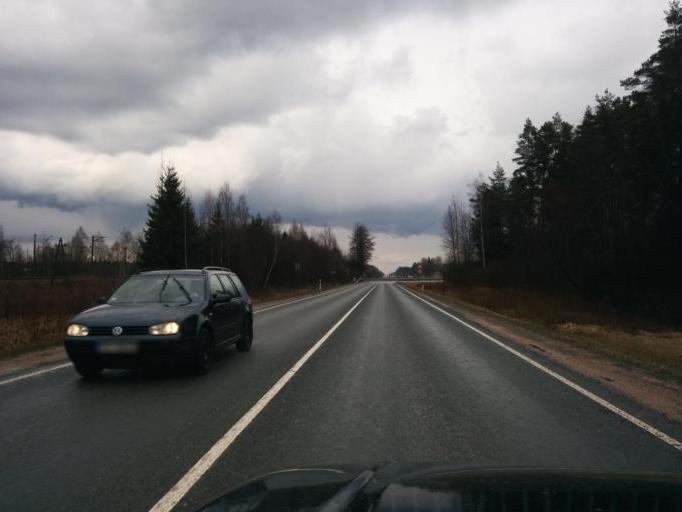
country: LV
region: Ozolnieku
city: Ozolnieki
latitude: 56.7258
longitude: 23.8524
